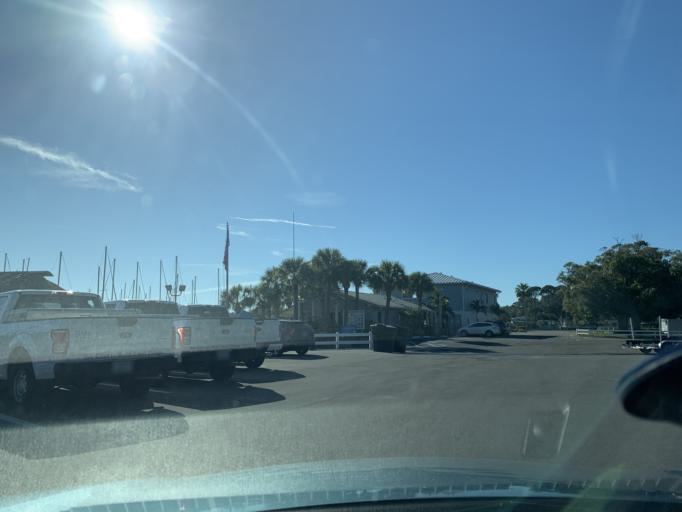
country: US
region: Florida
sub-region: Pinellas County
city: Gulfport
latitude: 27.7409
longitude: -82.6956
